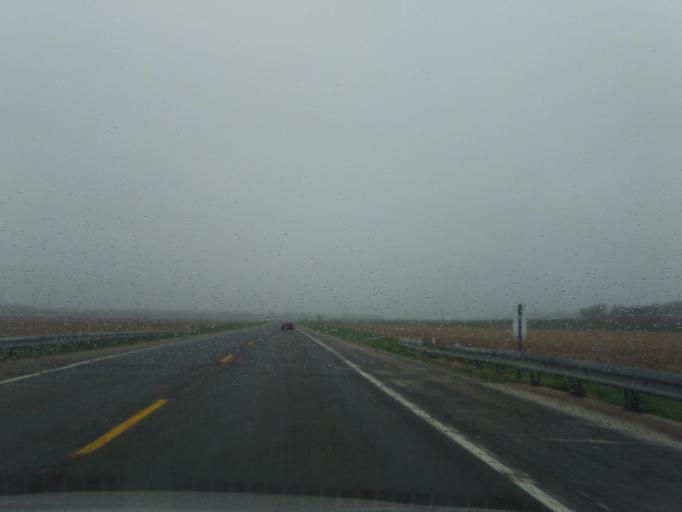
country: US
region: Nebraska
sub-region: Cuming County
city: Wisner
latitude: 41.9582
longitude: -96.8706
